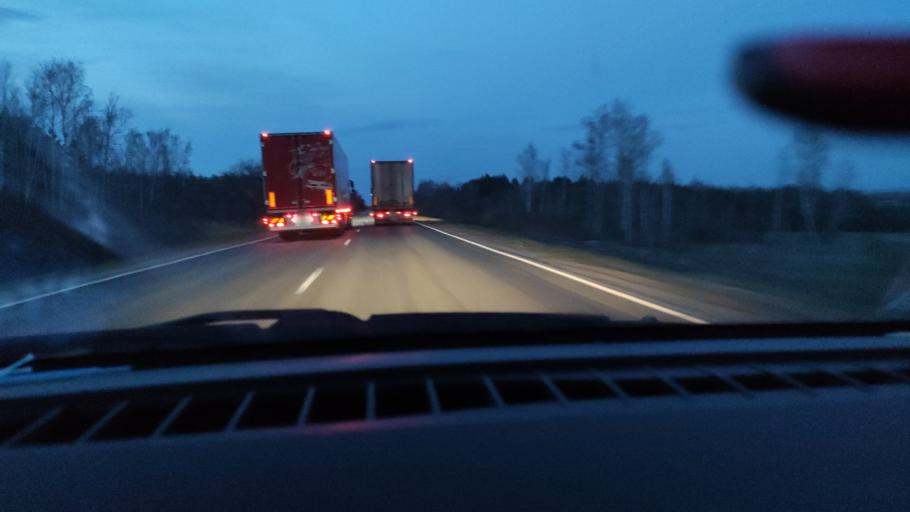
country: RU
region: Saratov
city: Sennoy
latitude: 52.1153
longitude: 46.8367
